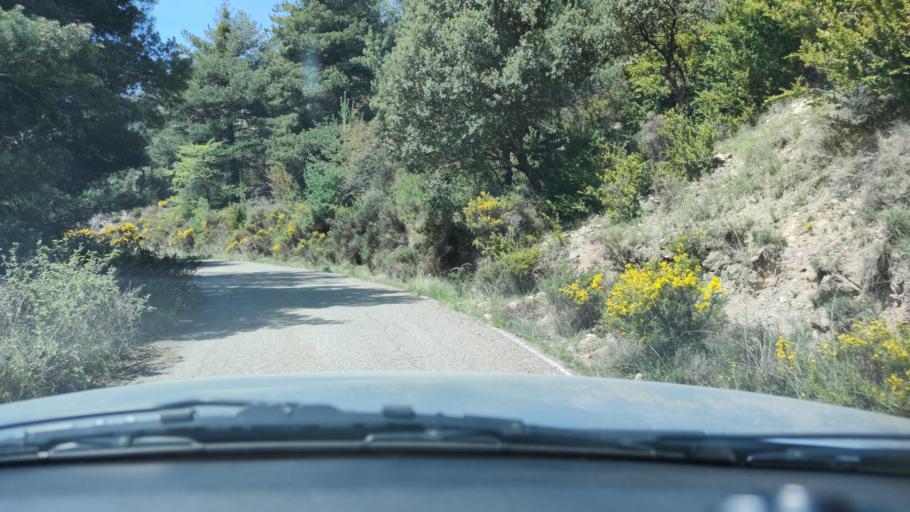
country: ES
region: Catalonia
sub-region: Provincia de Lleida
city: Sort
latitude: 42.3100
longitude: 1.1126
